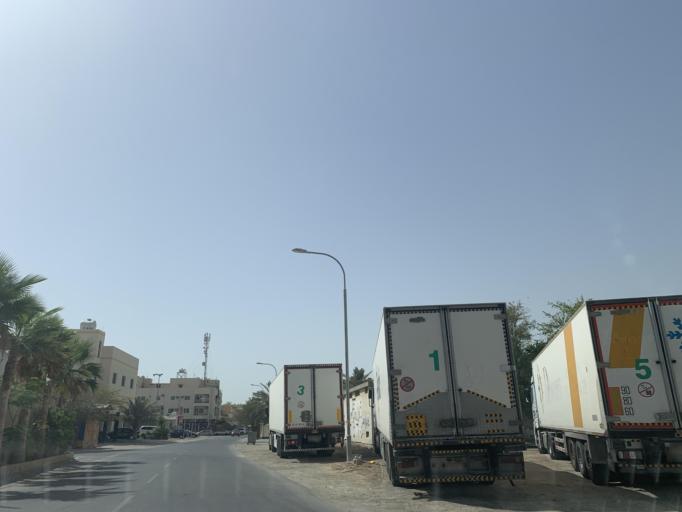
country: BH
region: Northern
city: Ar Rifa'
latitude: 26.1507
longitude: 50.5803
